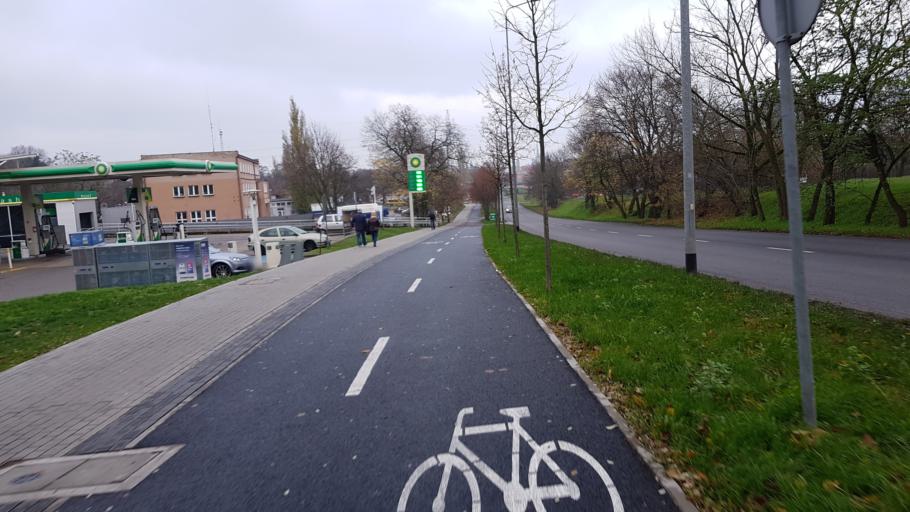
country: PL
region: West Pomeranian Voivodeship
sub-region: Szczecin
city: Szczecin
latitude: 53.4290
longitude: 14.5211
